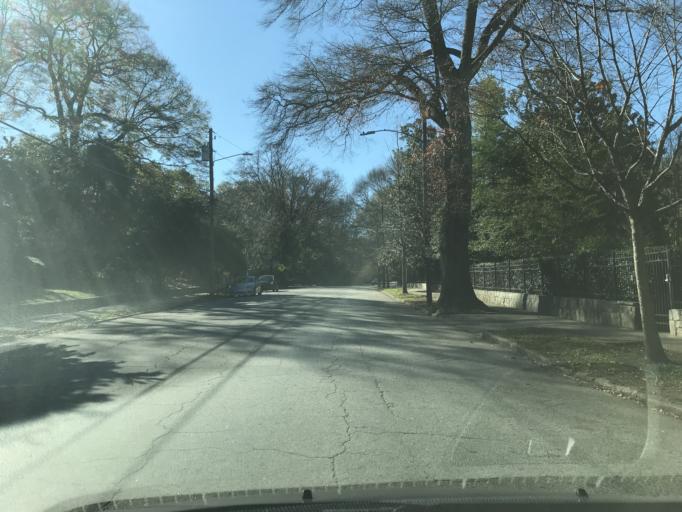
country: US
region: Georgia
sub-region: DeKalb County
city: Druid Hills
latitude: 33.7589
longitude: -84.3560
